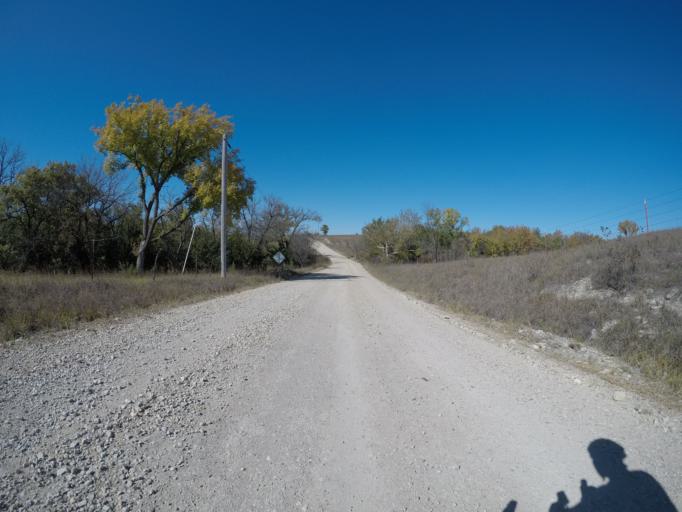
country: US
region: Kansas
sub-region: Wabaunsee County
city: Alma
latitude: 38.9753
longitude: -96.3642
